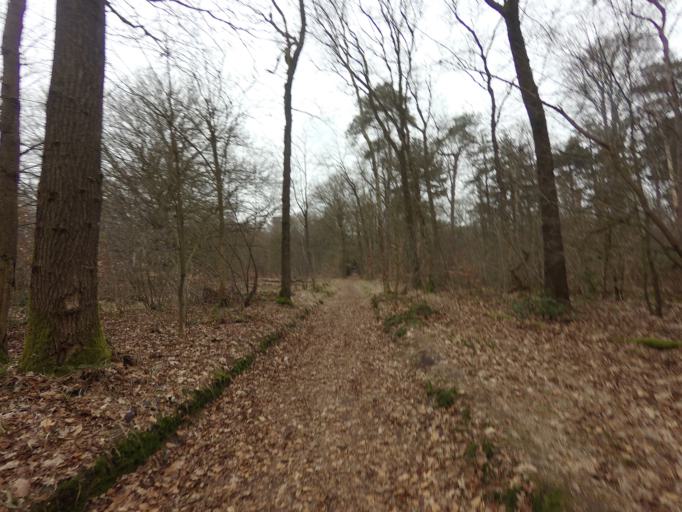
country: NL
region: Friesland
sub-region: Gemeente Gaasterlan-Sleat
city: Oudemirdum
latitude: 52.8561
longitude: 5.4872
